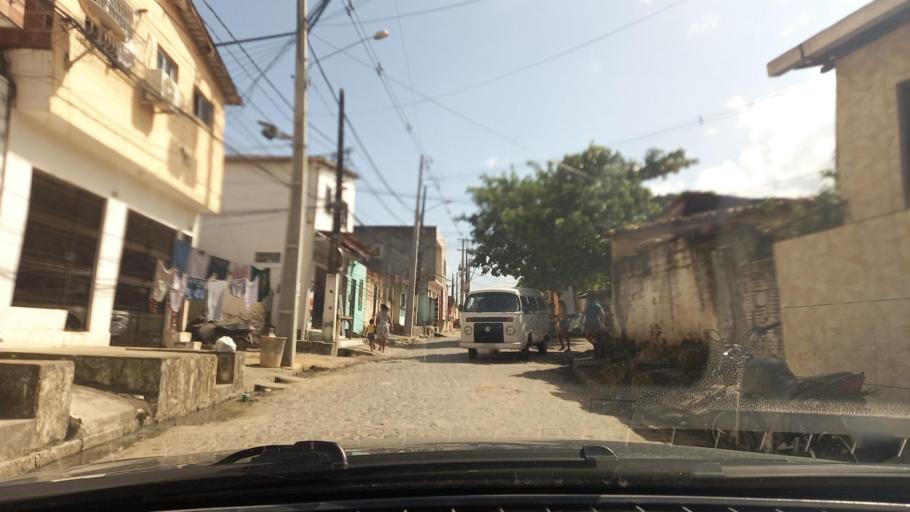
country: BR
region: Pernambuco
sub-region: Goiana
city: Goiana
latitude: -7.5663
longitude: -35.0106
